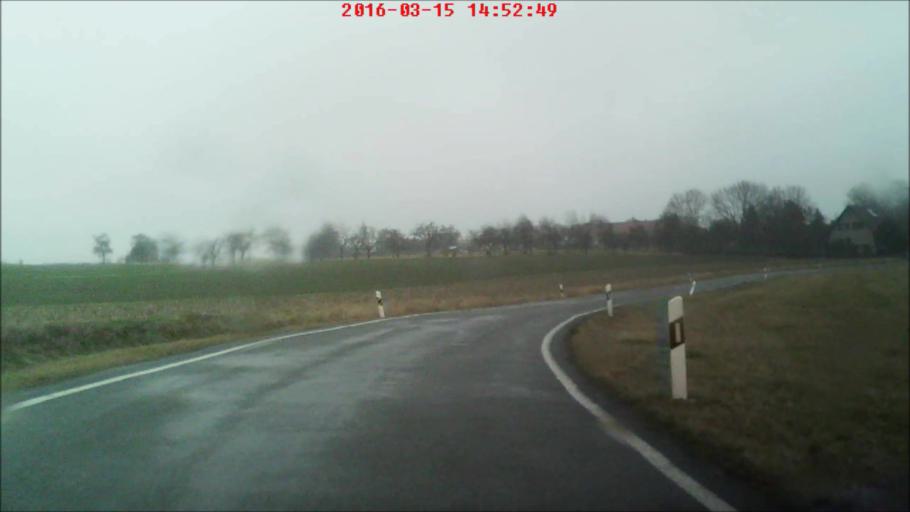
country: DE
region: Thuringia
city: Rockhausen
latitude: 50.9171
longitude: 11.0445
